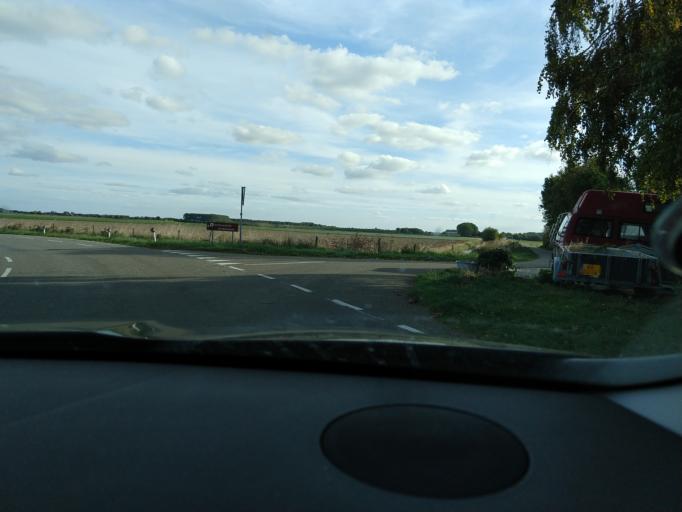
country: NL
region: Zeeland
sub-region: Gemeente Noord-Beveland
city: Kamperland
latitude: 51.5798
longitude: 3.6757
